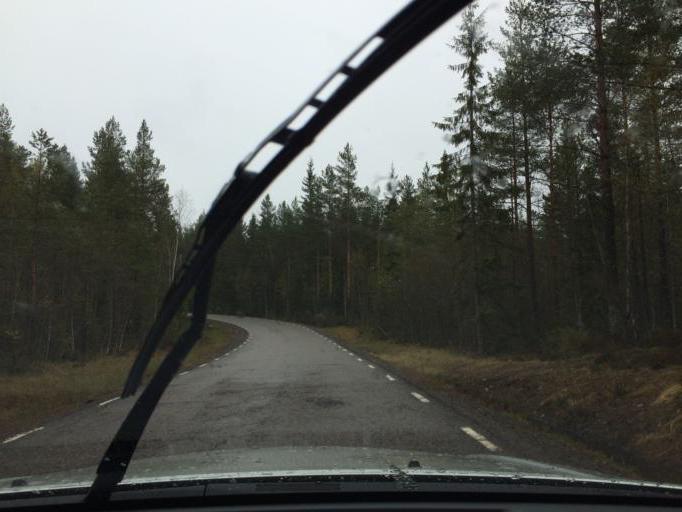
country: SE
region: Dalarna
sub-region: Ludvika Kommun
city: Abborrberget
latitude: 60.0440
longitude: 14.7463
